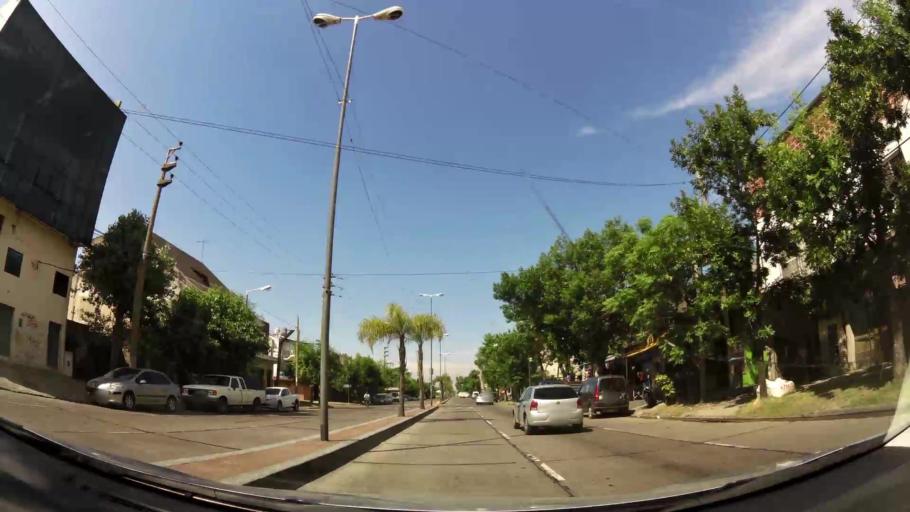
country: AR
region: Buenos Aires
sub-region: Partido de Tigre
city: Tigre
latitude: -34.4682
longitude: -58.5882
